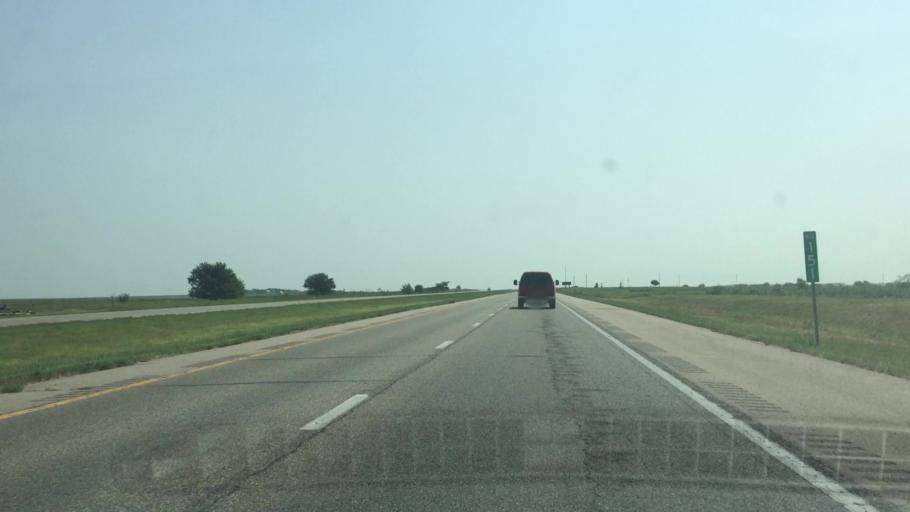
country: US
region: Kansas
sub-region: Osage County
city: Osage City
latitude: 38.4258
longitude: -95.8102
